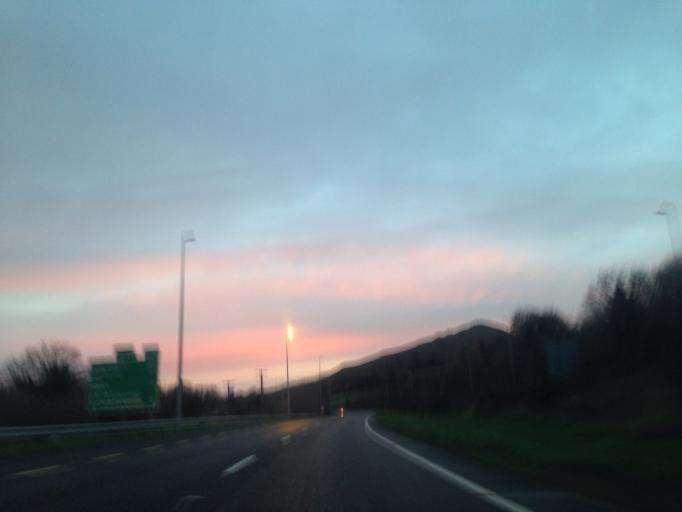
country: IE
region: Leinster
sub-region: Wicklow
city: Kilmacanoge
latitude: 53.1486
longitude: -6.1251
